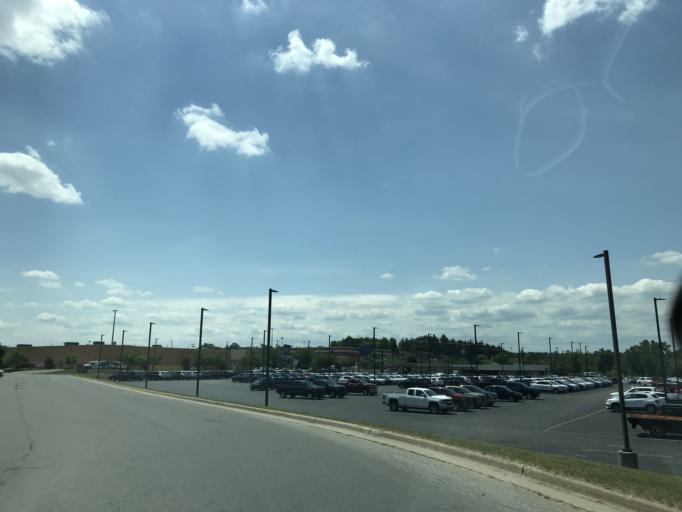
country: US
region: Michigan
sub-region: Grand Traverse County
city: Traverse City
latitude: 44.7258
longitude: -85.6430
